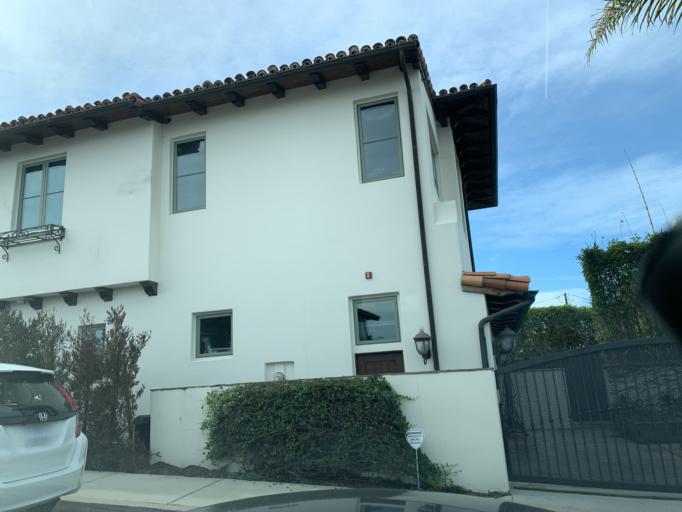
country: US
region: California
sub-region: Los Angeles County
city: Manhattan Beach
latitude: 33.8851
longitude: -118.4021
